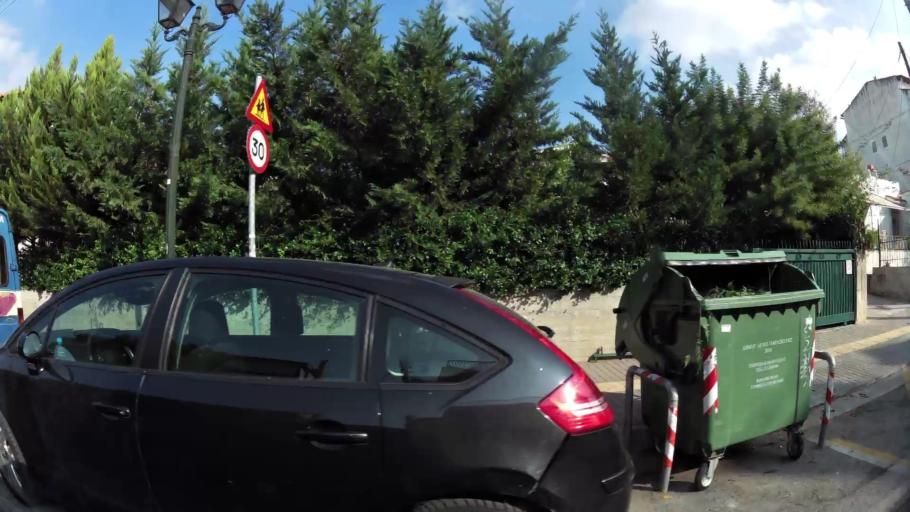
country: GR
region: Attica
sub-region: Nomarchia Athinas
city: Cholargos
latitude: 38.0056
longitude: 23.8124
